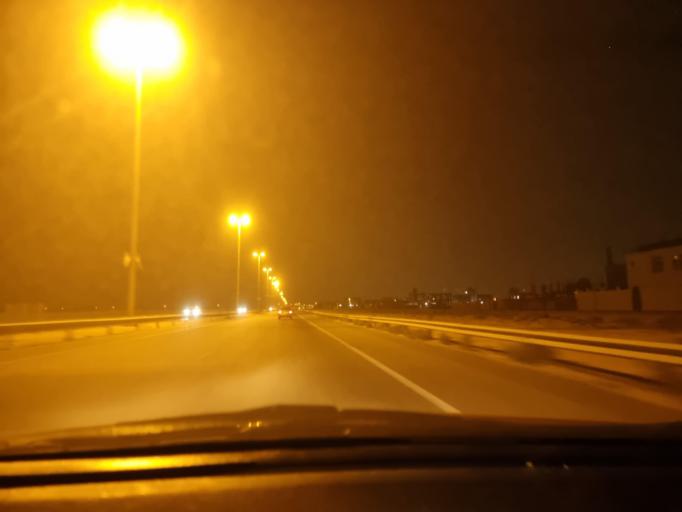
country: AE
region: Abu Dhabi
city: Abu Dhabi
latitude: 24.3728
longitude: 54.6731
